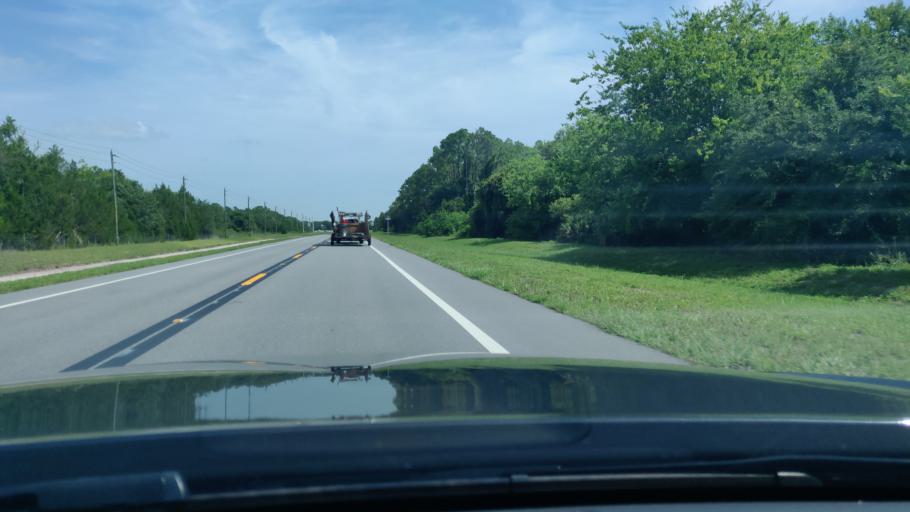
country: US
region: Florida
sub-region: Flagler County
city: Flagler Beach
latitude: 29.5110
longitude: -81.1622
